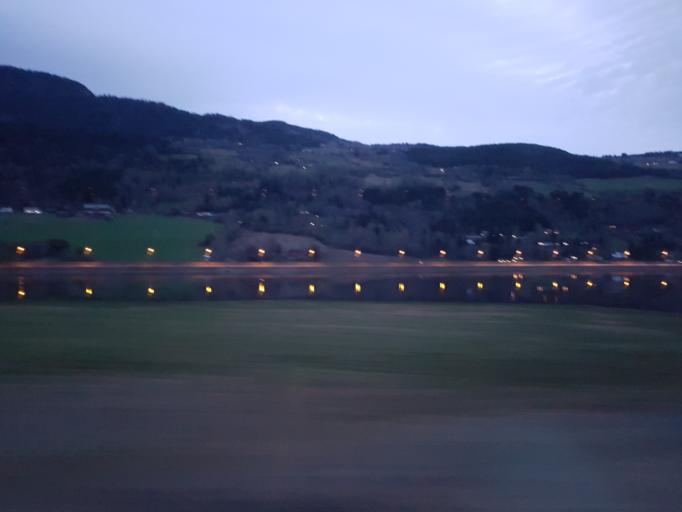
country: NO
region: Oppland
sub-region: Oyer
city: Tretten
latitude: 61.2746
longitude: 10.3724
